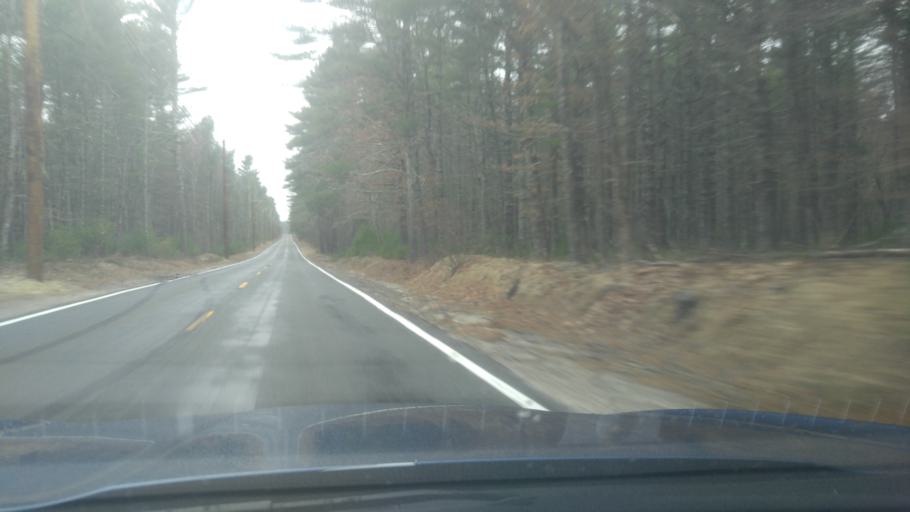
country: US
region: Rhode Island
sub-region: Kent County
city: West Greenwich
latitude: 41.6472
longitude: -71.5912
